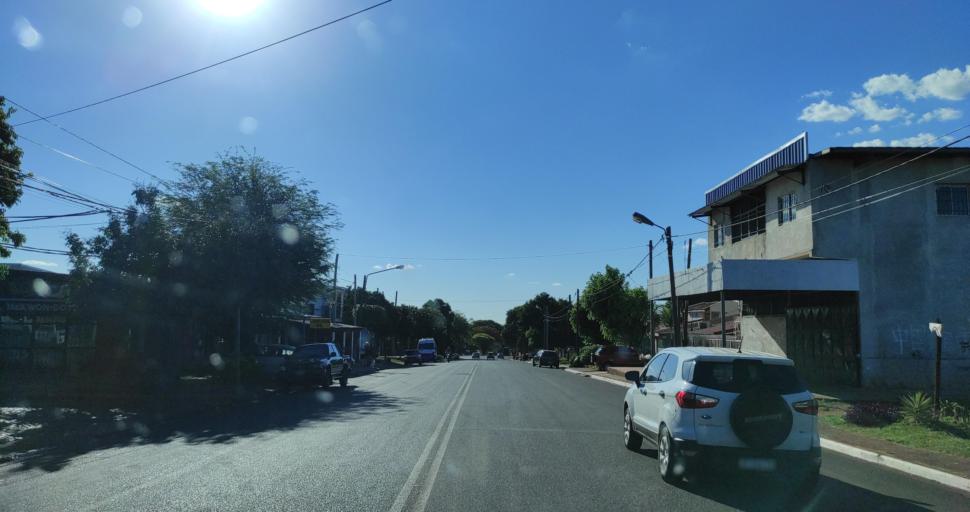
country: AR
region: Misiones
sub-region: Departamento de Capital
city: Posadas
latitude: -27.3779
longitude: -55.9274
